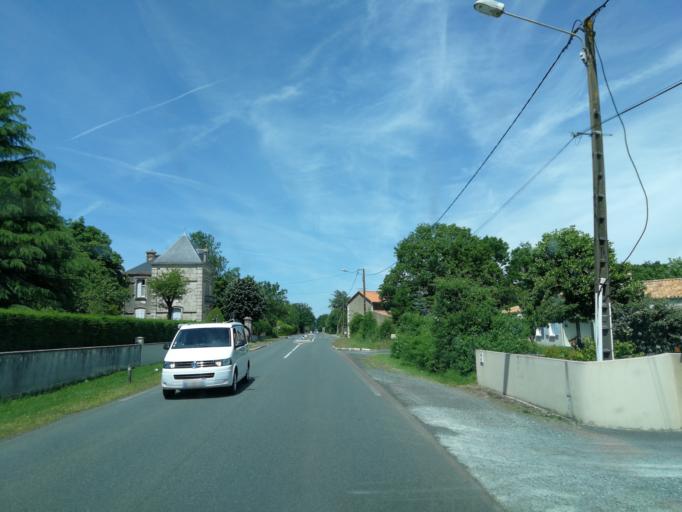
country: FR
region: Pays de la Loire
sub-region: Departement de la Vendee
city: Pissotte
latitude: 46.5286
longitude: -0.8075
